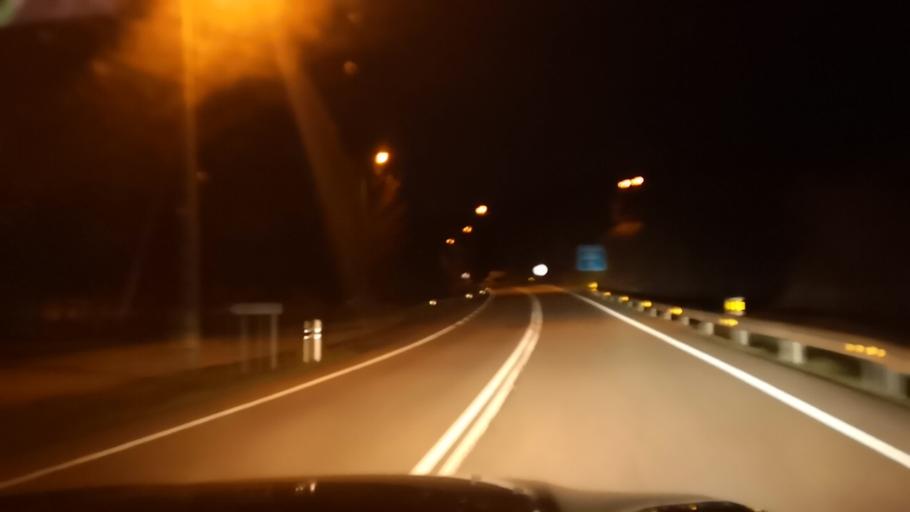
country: ES
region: Galicia
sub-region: Provincia de Ourense
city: Cualedro
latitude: 41.9696
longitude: -7.5199
